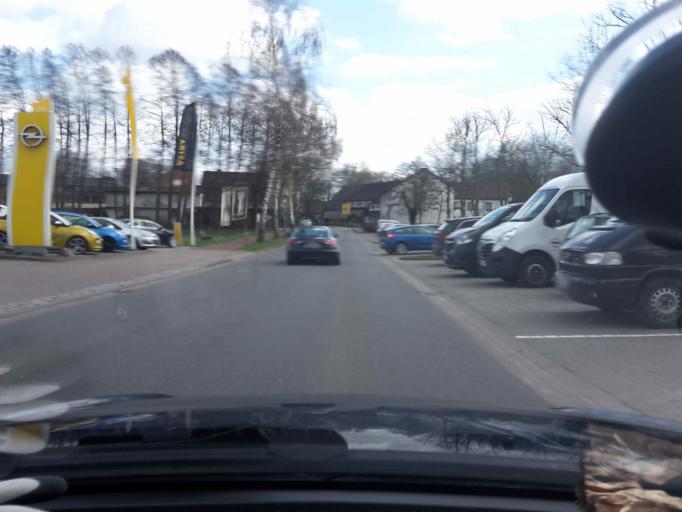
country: DE
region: Lower Saxony
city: Hanstedt
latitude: 53.2578
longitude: 10.0165
